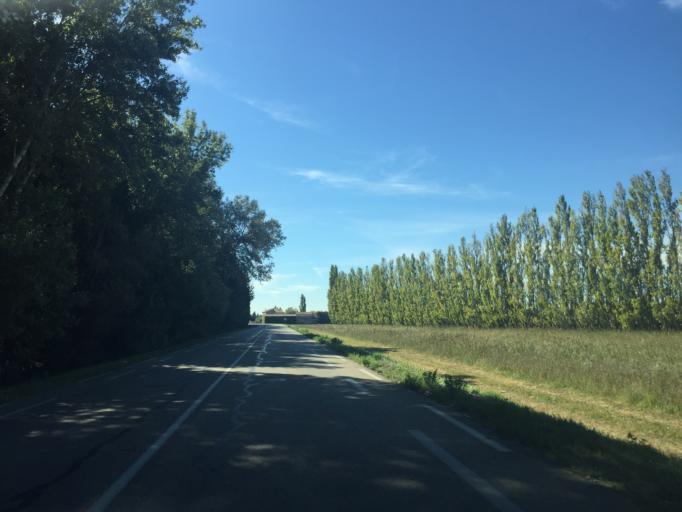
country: FR
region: Provence-Alpes-Cote d'Azur
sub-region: Departement du Vaucluse
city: Orange
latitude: 44.1316
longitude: 4.7835
